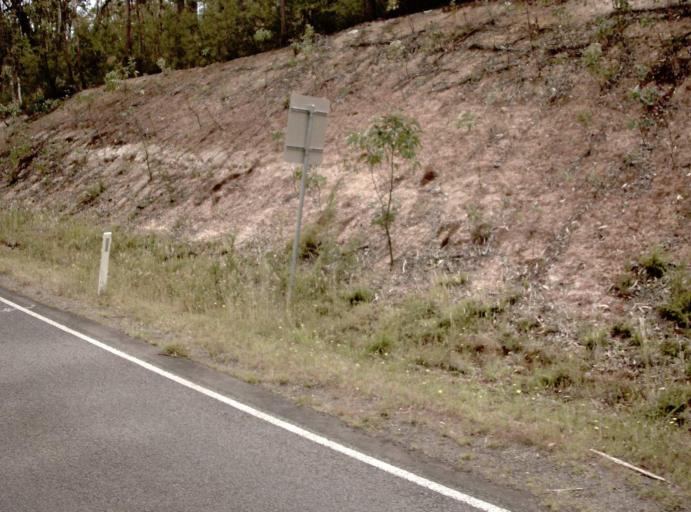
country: AU
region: Victoria
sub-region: Latrobe
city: Traralgon
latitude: -38.0728
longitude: 146.4310
